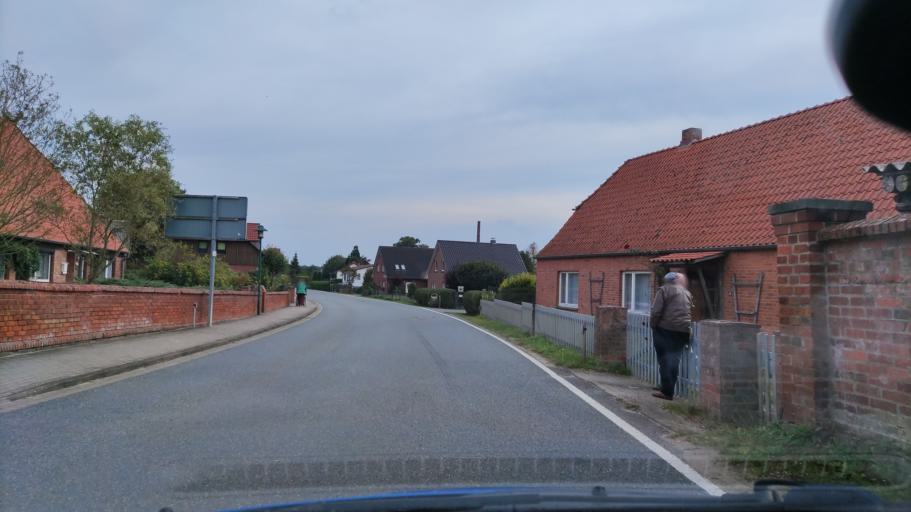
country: DE
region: Lower Saxony
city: Neu Darchau
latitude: 53.2800
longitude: 10.9327
